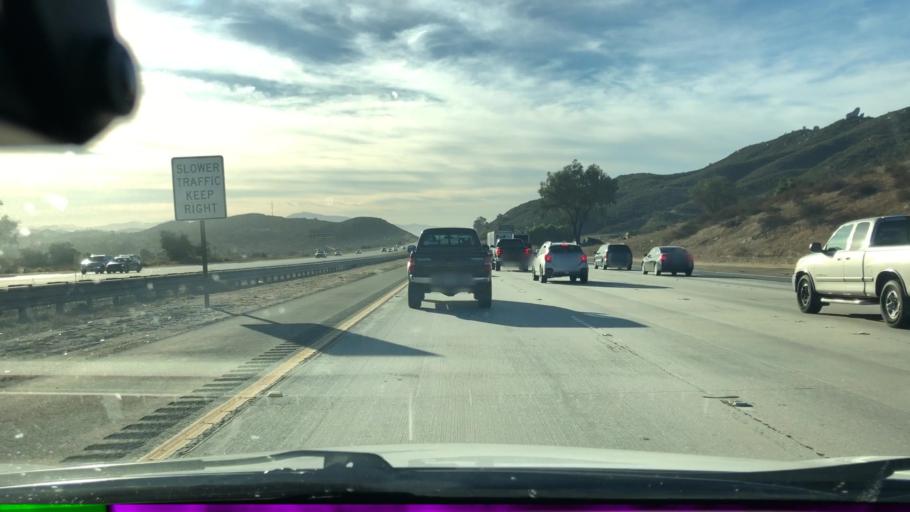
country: US
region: California
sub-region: San Diego County
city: Hidden Meadows
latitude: 33.1805
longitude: -117.1162
